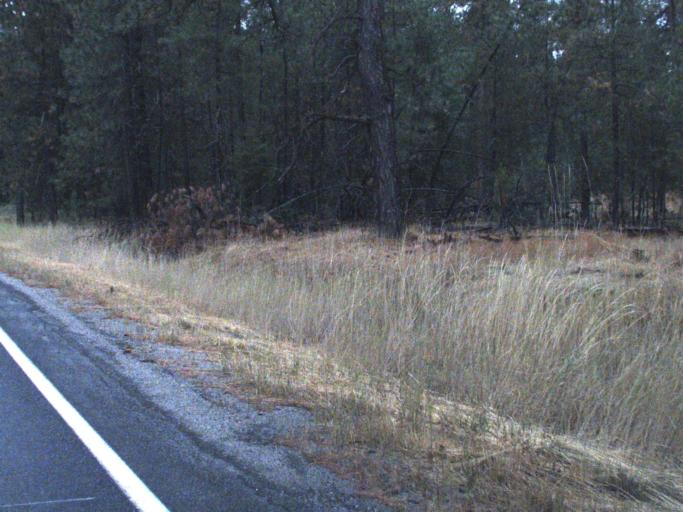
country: US
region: Washington
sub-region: Stevens County
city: Chewelah
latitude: 48.0384
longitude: -117.7361
